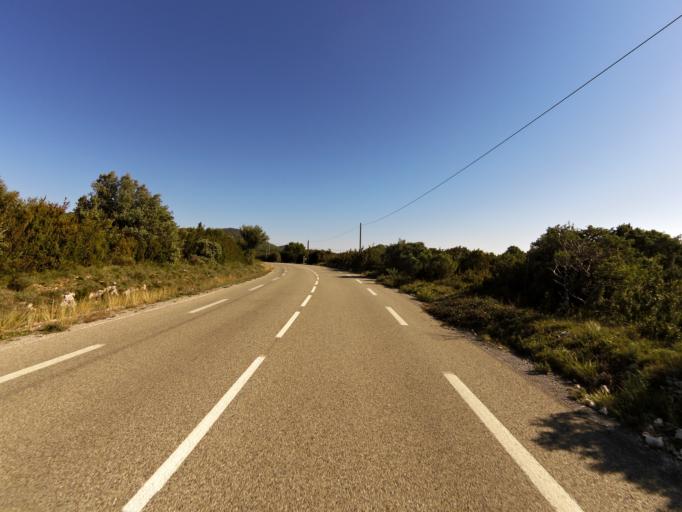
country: FR
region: Rhone-Alpes
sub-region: Departement de l'Ardeche
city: Ruoms
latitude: 44.4016
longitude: 4.4545
